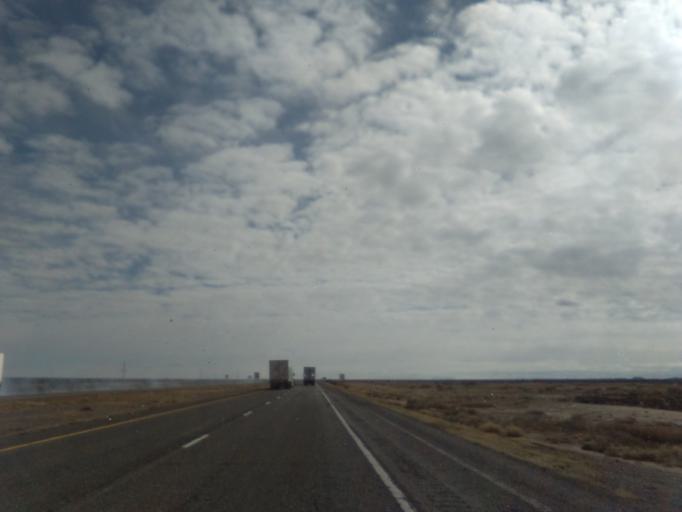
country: US
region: New Mexico
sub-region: Hidalgo County
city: Lordsburg
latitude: 32.3091
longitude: -108.6023
